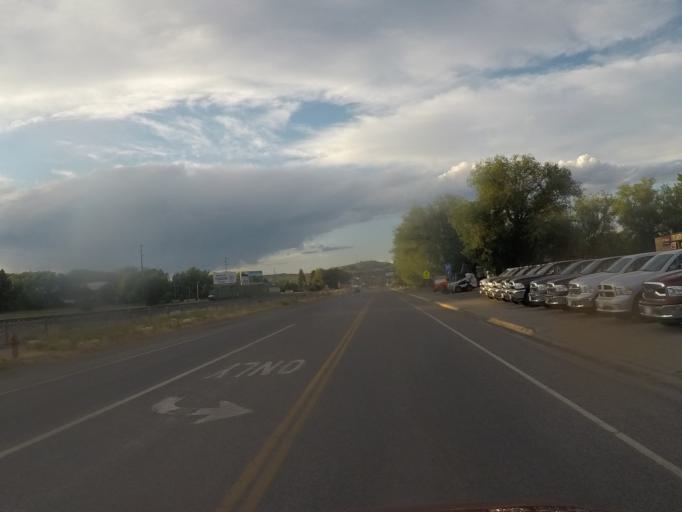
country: US
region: Montana
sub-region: Park County
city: Livingston
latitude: 45.6492
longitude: -110.5725
